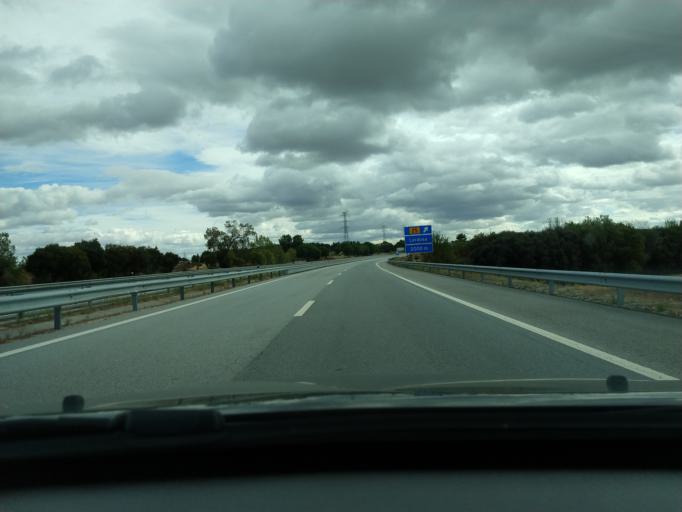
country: PT
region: Guarda
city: Alcains
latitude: 40.0077
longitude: -7.4642
